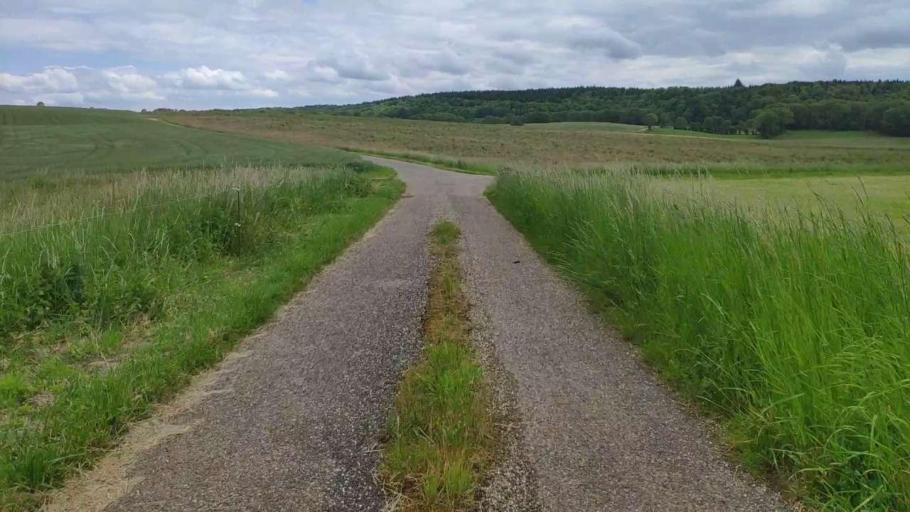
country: FR
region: Franche-Comte
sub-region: Departement du Jura
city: Poligny
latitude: 46.7603
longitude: 5.6444
